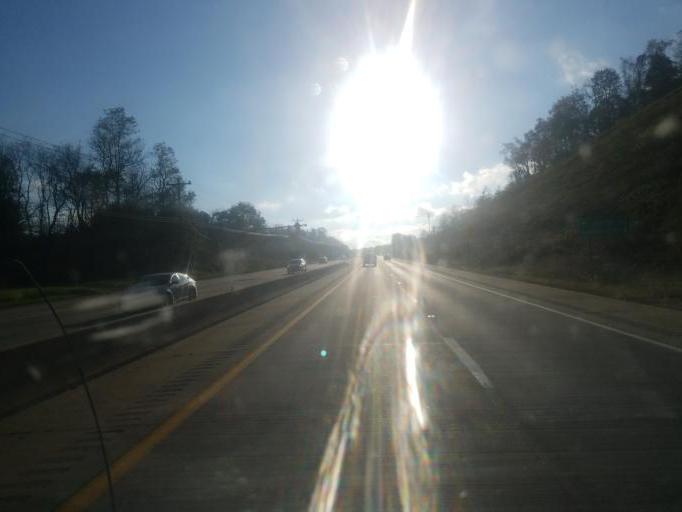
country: US
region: Pennsylvania
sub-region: Westmoreland County
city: Murrysville
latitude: 40.4171
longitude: -79.6468
